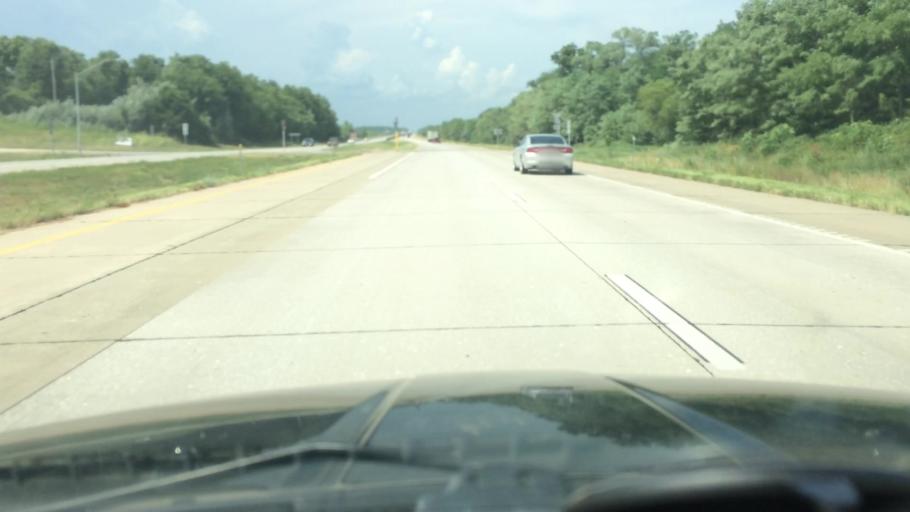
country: US
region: Missouri
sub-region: Henry County
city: Clinton
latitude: 38.2635
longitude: -93.7602
